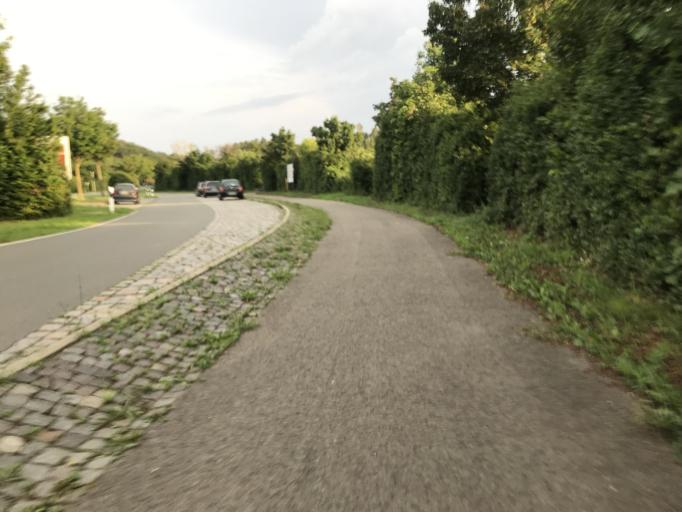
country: DE
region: Saxony-Anhalt
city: Quedlinburg
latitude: 51.8062
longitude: 11.1301
